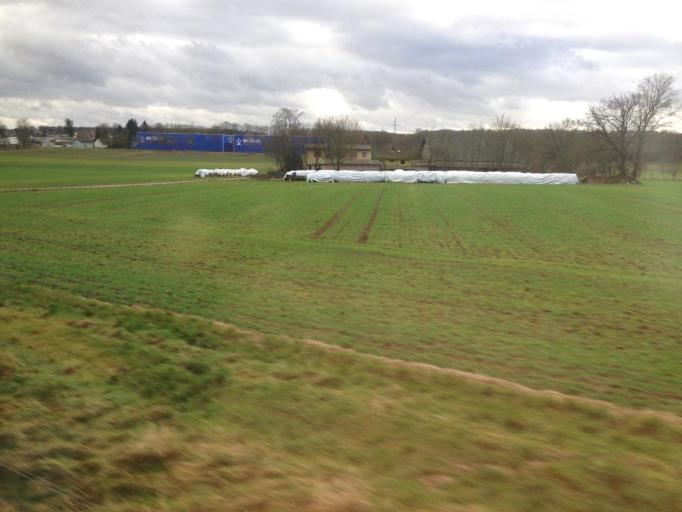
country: DE
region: Hesse
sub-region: Regierungsbezirk Giessen
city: Hungen
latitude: 50.4821
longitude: 8.8806
